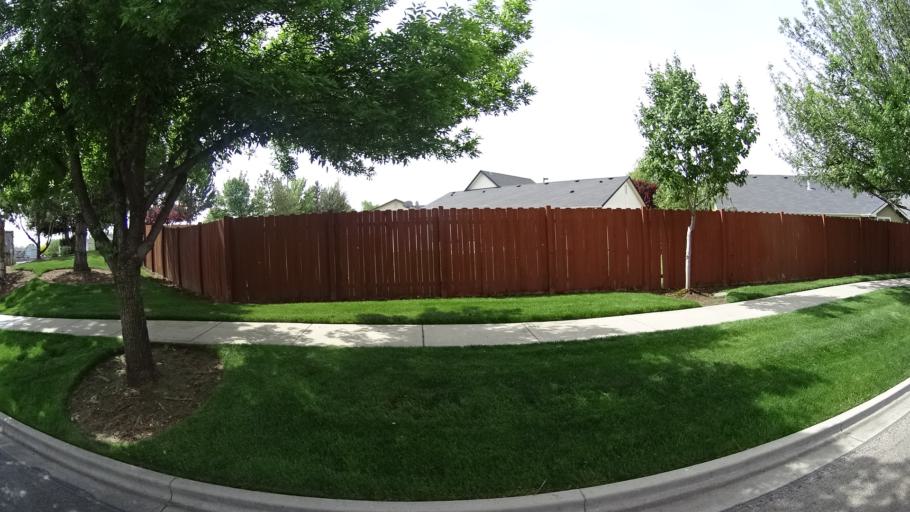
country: US
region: Idaho
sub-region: Ada County
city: Meridian
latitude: 43.5517
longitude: -116.3350
